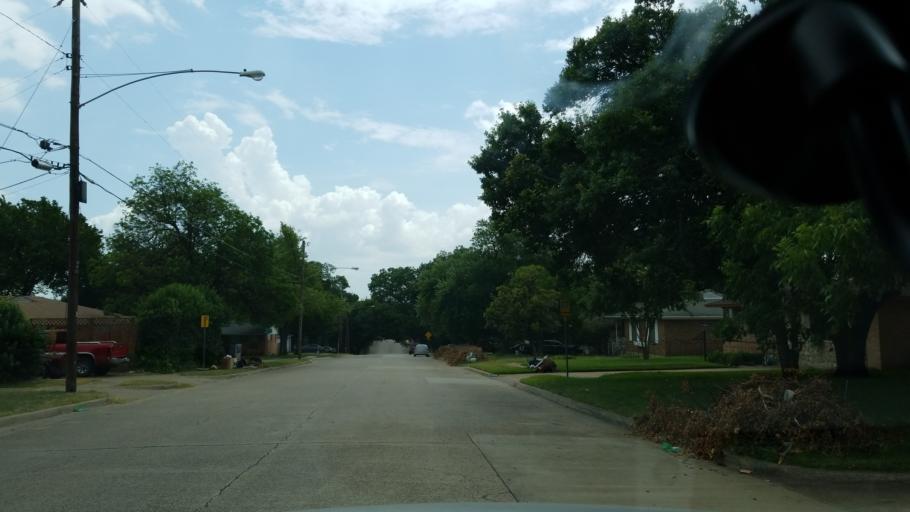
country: US
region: Texas
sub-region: Dallas County
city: Cockrell Hill
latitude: 32.6862
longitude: -96.8529
